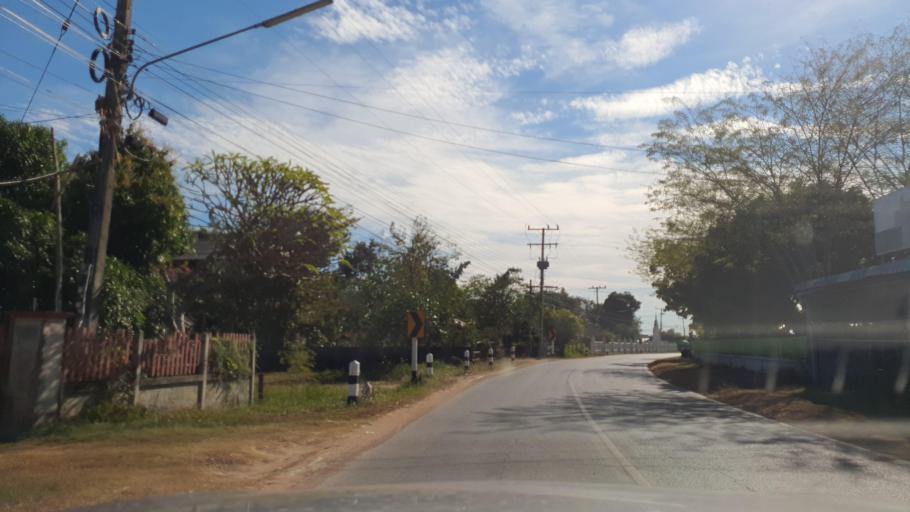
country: TH
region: Kalasin
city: Kuchinarai
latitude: 16.5467
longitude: 104.0954
